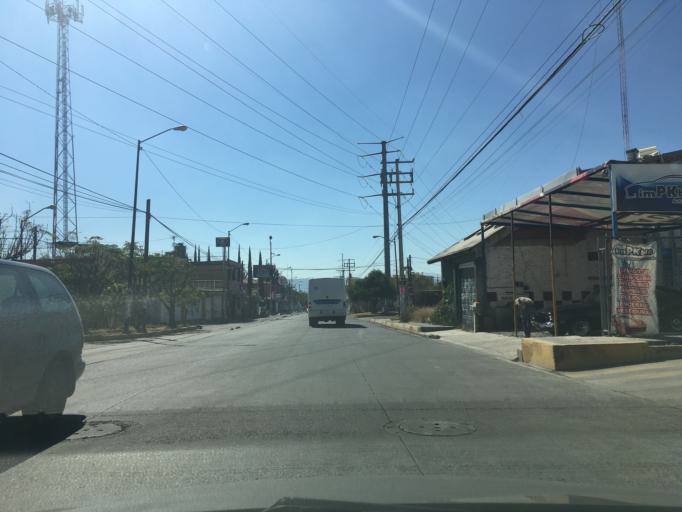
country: MX
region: Michoacan
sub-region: Morelia
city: San Antonio
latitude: 19.6940
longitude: -101.2504
